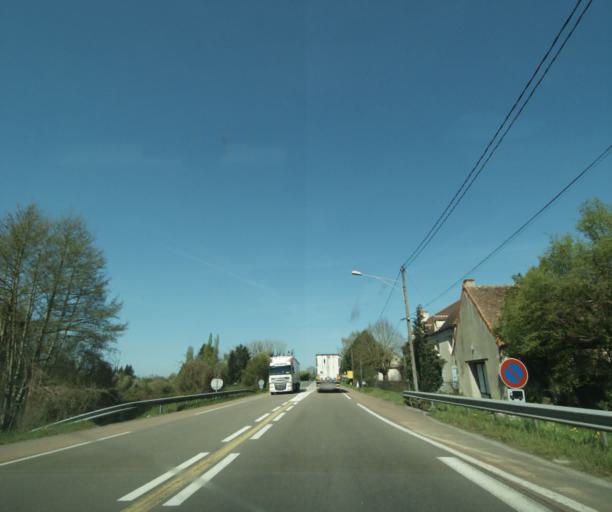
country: FR
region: Bourgogne
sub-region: Departement de la Nievre
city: Chantenay-Saint-Imbert
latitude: 46.7305
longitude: 3.1711
